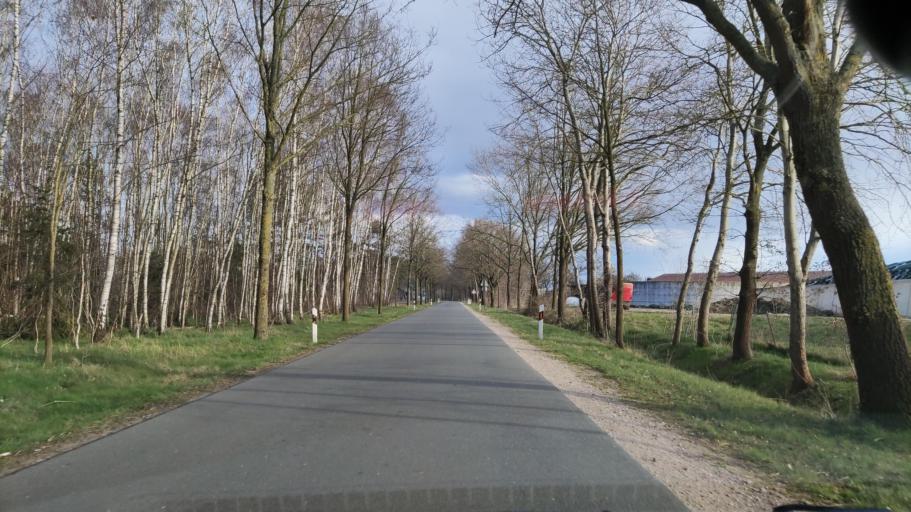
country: DE
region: Lower Saxony
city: Trebel
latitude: 53.0326
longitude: 11.2612
